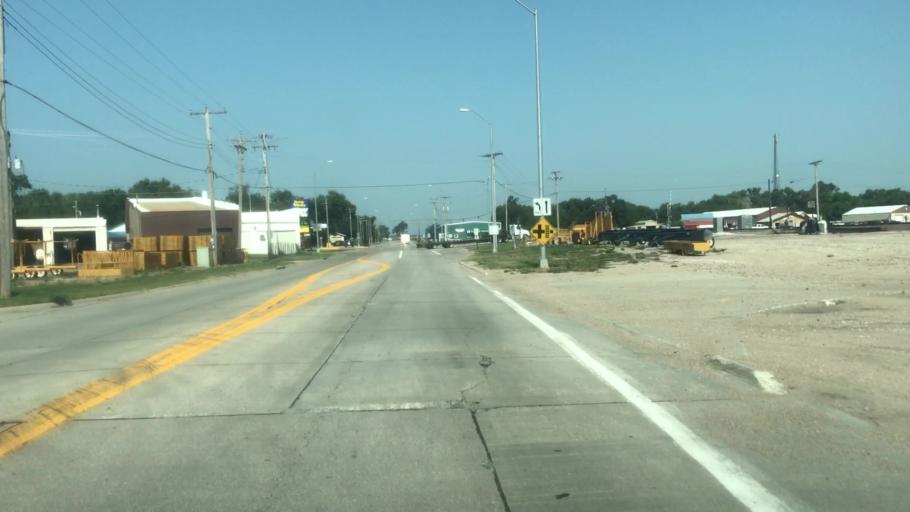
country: US
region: Nebraska
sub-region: Hall County
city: Wood River
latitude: 41.0016
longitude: -98.6059
